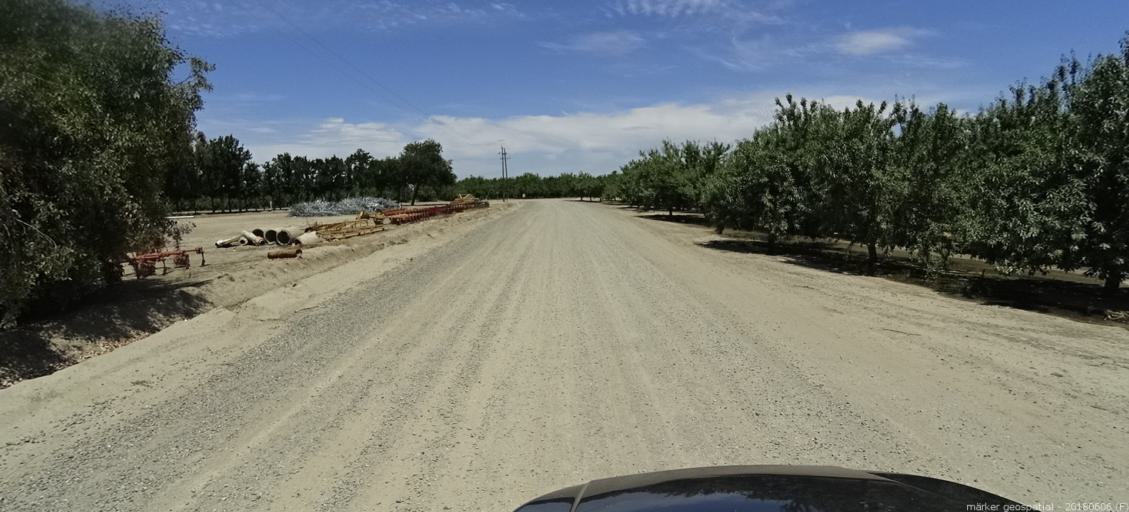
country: US
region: California
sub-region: Fresno County
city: Mendota
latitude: 36.8050
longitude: -120.3501
